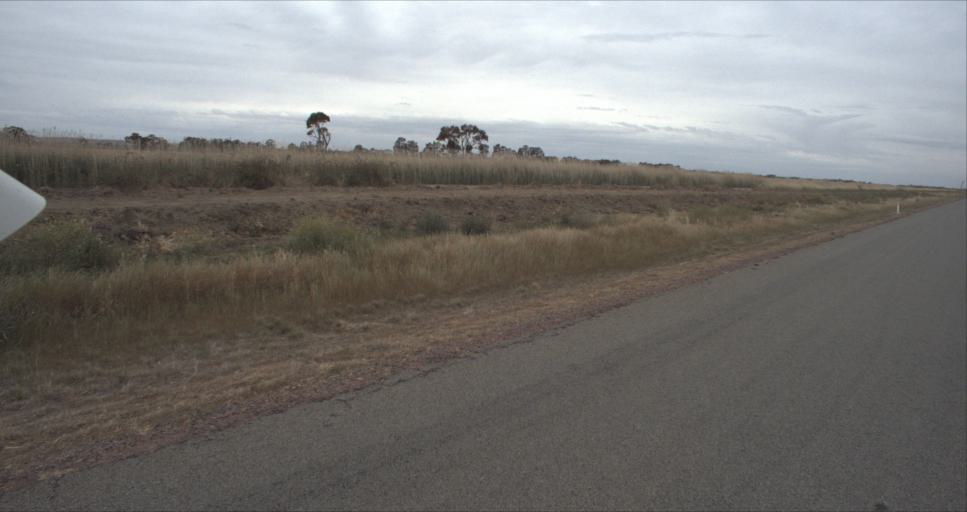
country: AU
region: New South Wales
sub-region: Leeton
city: Leeton
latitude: -34.4873
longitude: 146.4022
